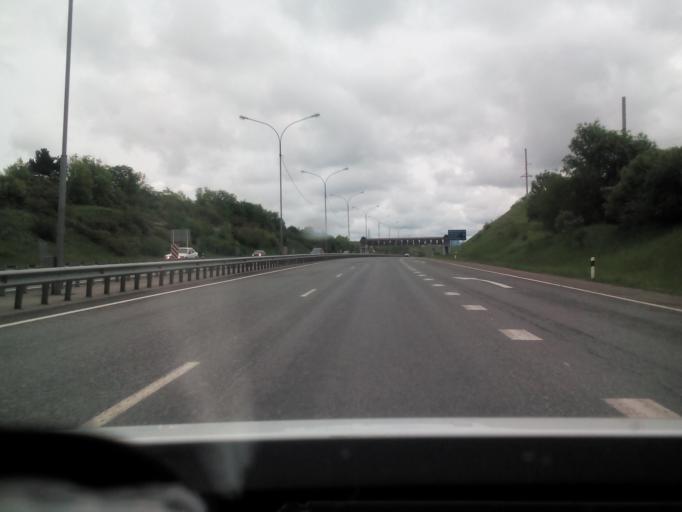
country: RU
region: Stavropol'skiy
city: Yasnaya Polyana
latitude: 44.0183
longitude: 42.8035
